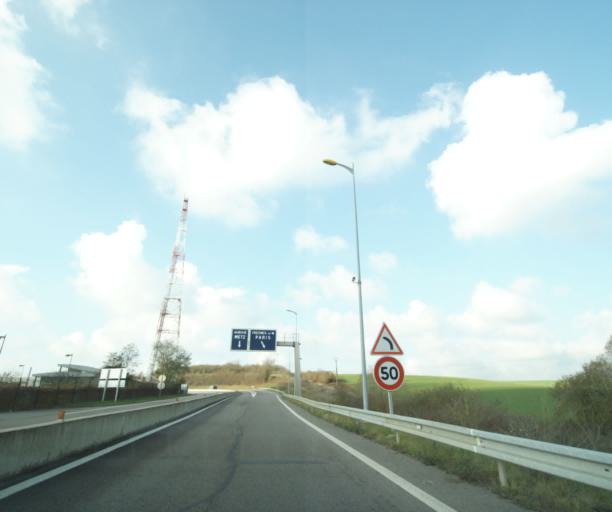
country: FR
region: Lorraine
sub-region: Departement de Meurthe-et-Moselle
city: Giraumont
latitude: 49.2000
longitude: 5.9010
